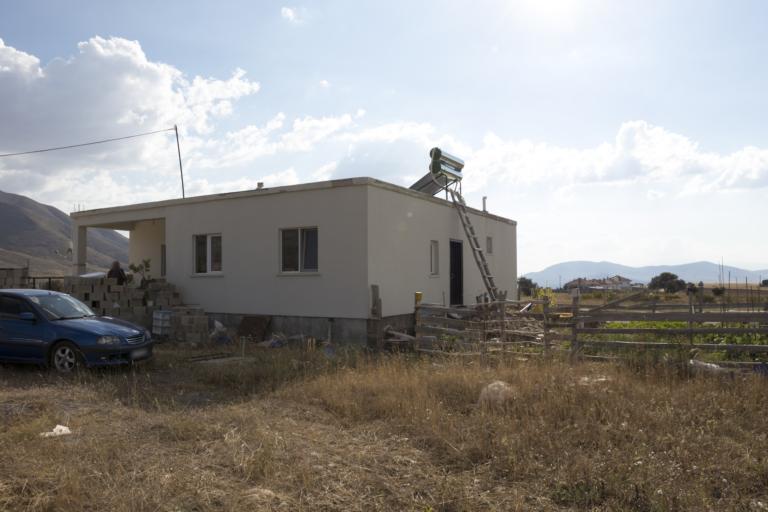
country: TR
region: Kayseri
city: Toklar
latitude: 38.4092
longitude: 36.0754
